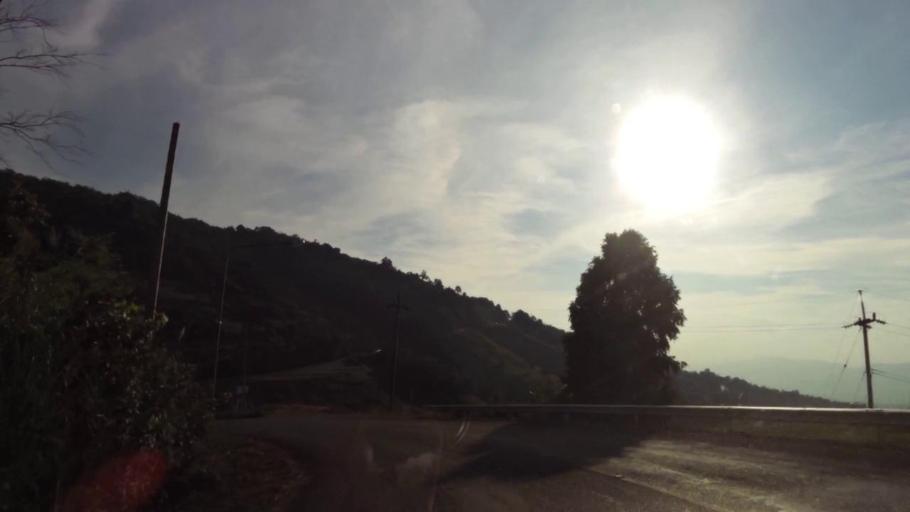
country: TH
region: Chiang Rai
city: Khun Tan
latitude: 19.8655
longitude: 100.4404
